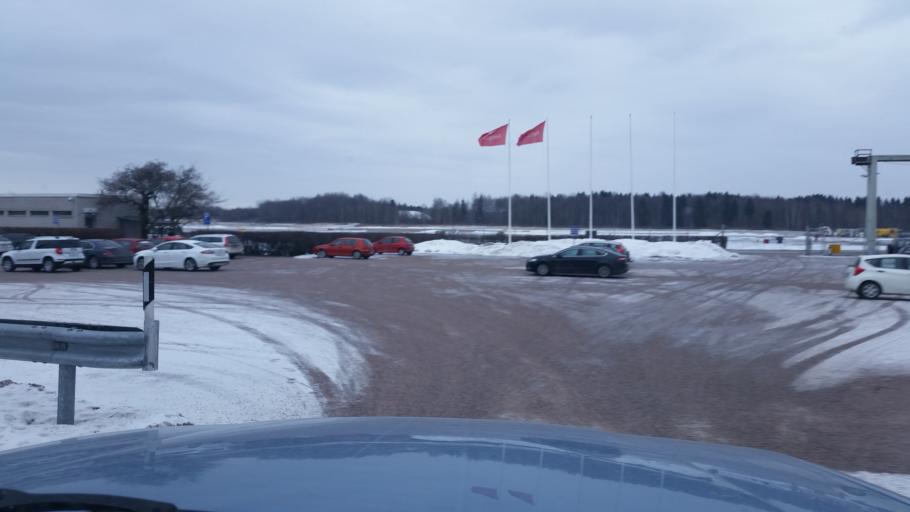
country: FI
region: Uusimaa
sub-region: Helsinki
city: Vantaa
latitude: 60.2487
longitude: 25.0464
